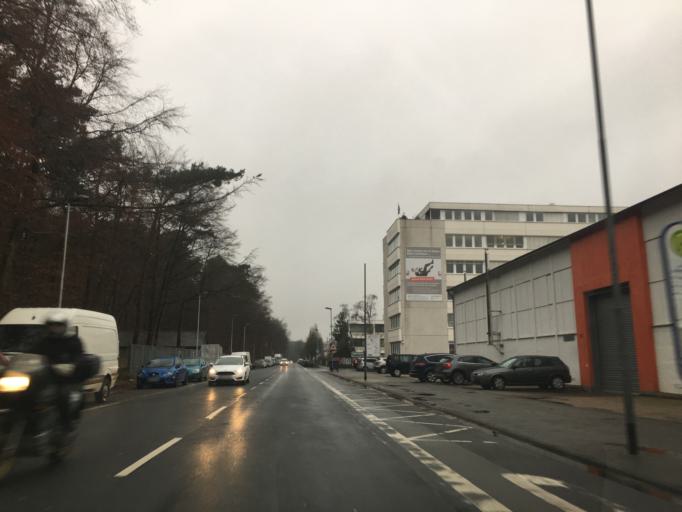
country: DE
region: Hesse
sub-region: Regierungsbezirk Darmstadt
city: Neu Isenburg
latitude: 50.0419
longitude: 8.6891
